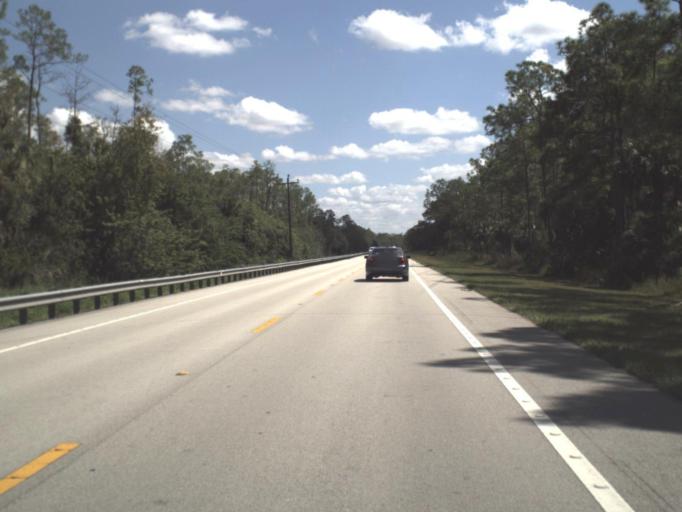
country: US
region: Florida
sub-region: Collier County
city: Lely Resort
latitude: 26.0009
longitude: -81.6020
